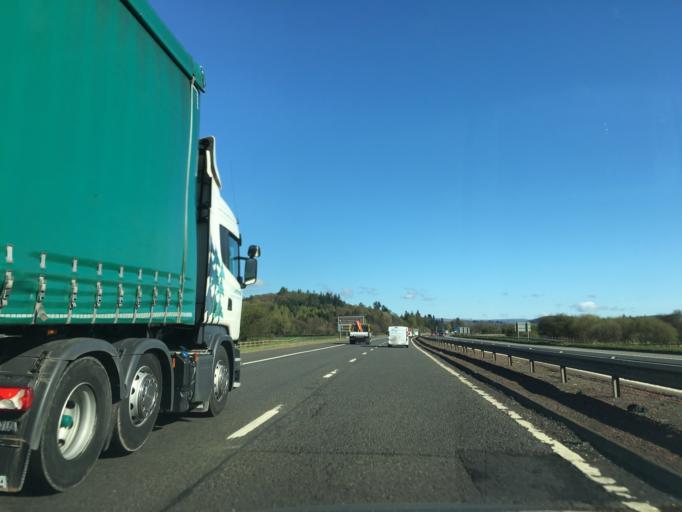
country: GB
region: Scotland
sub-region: Stirling
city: Stirling
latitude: 56.1214
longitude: -3.9701
